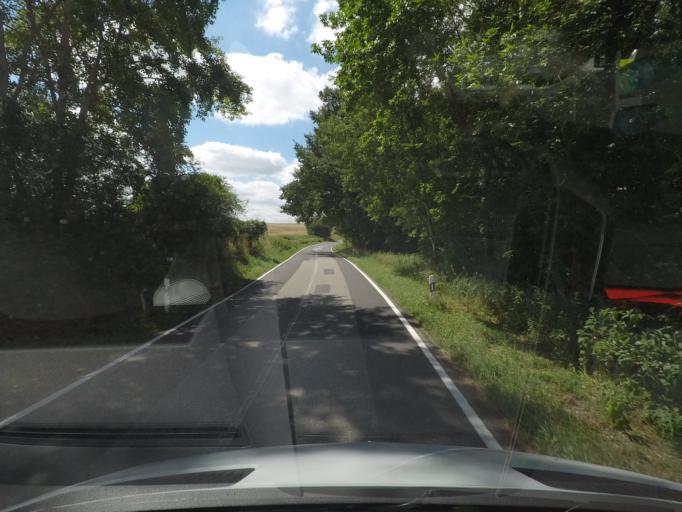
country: DE
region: Brandenburg
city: Brussow
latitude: 53.3137
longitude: 14.1171
